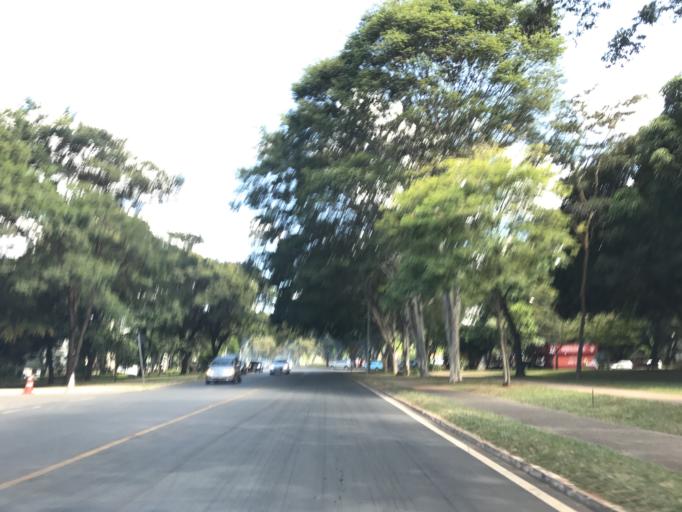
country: BR
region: Federal District
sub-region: Brasilia
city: Brasilia
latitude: -15.8346
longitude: -47.9192
